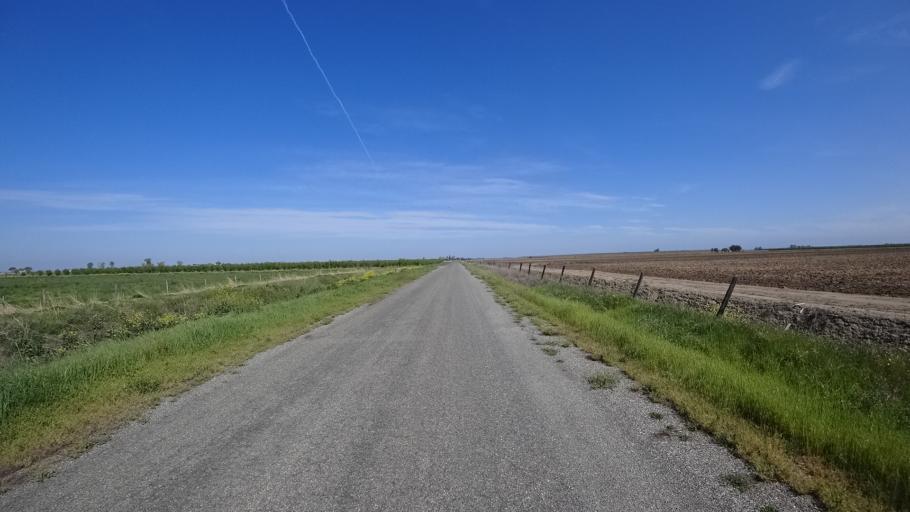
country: US
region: California
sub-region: Glenn County
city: Hamilton City
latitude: 39.6077
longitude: -122.0557
